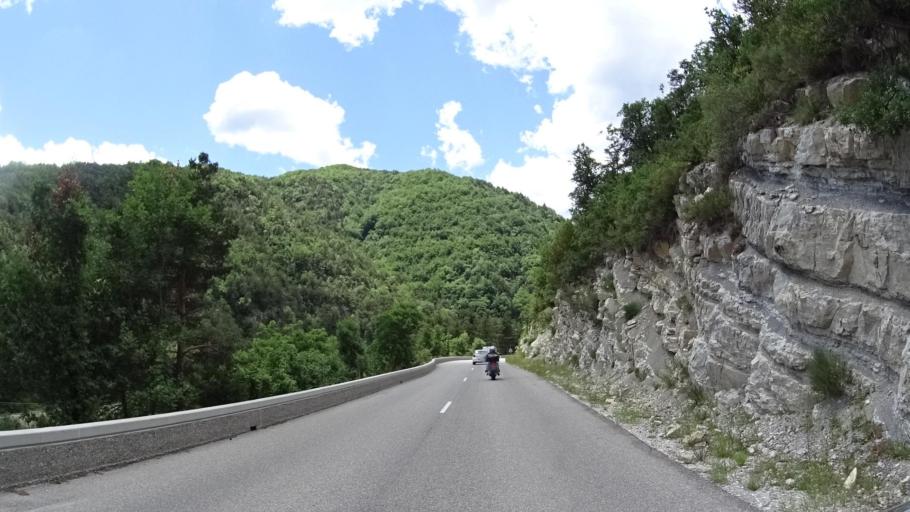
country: FR
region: Provence-Alpes-Cote d'Azur
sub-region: Departement des Alpes-de-Haute-Provence
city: Annot
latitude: 44.0089
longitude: 6.5597
